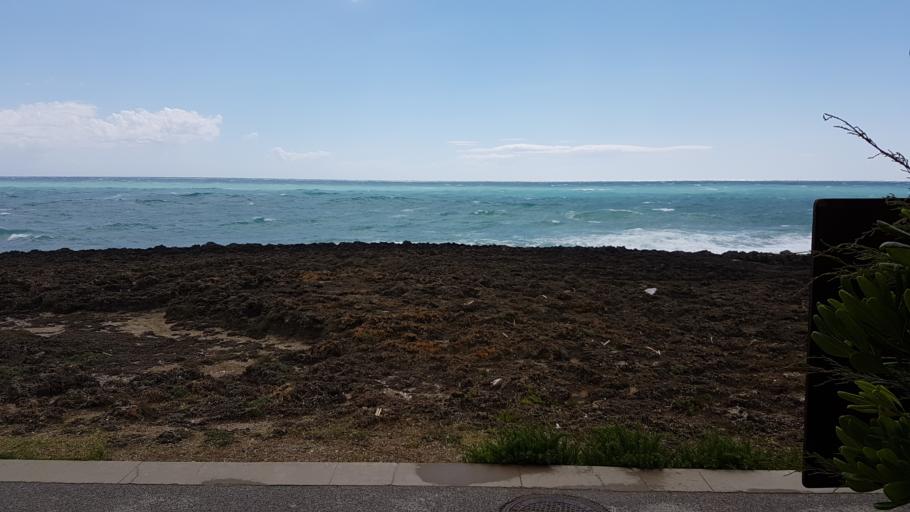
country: IT
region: Tuscany
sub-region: Provincia di Livorno
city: Rosignano Solvay-Castiglioncello
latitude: 43.4006
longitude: 10.4221
